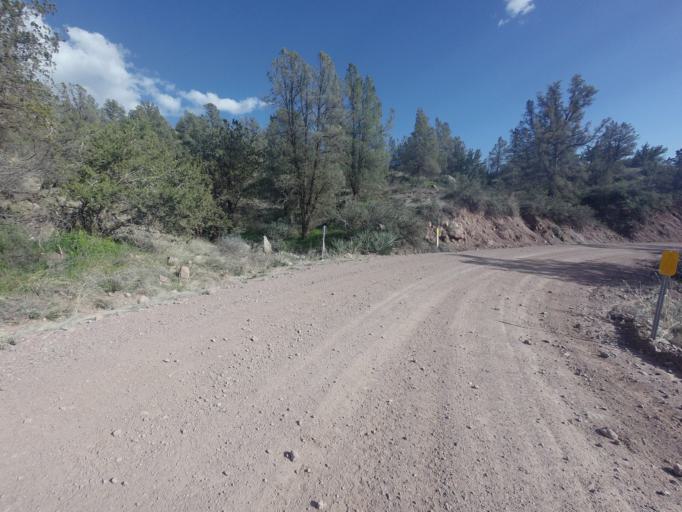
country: US
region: Arizona
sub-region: Gila County
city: Pine
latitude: 34.3979
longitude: -111.6565
